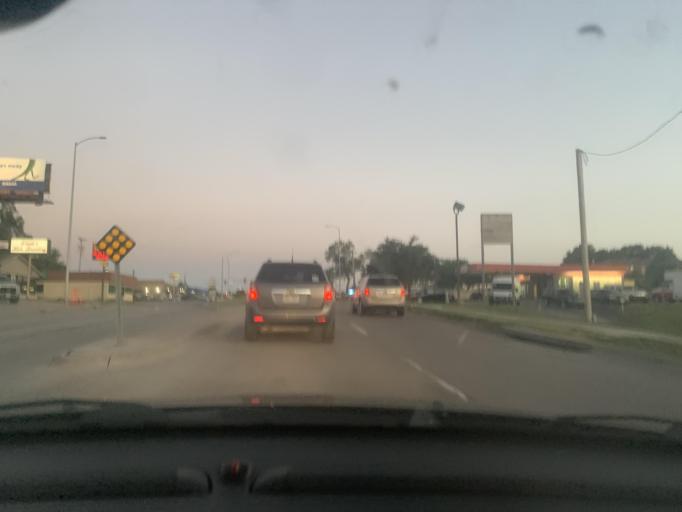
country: US
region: Nebraska
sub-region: Douglas County
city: Ralston
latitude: 41.2833
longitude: -96.0526
